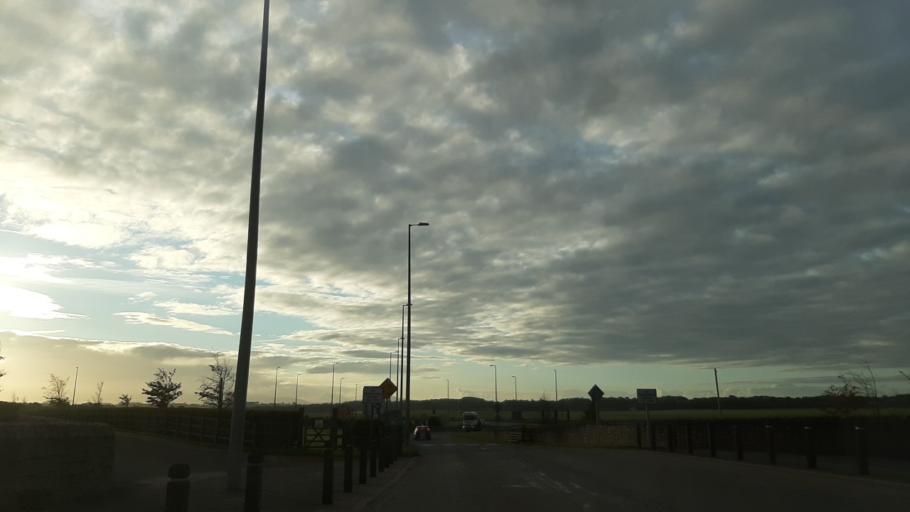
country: IE
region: Leinster
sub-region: Kildare
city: Athgarvan
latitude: 53.1673
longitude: -6.8388
